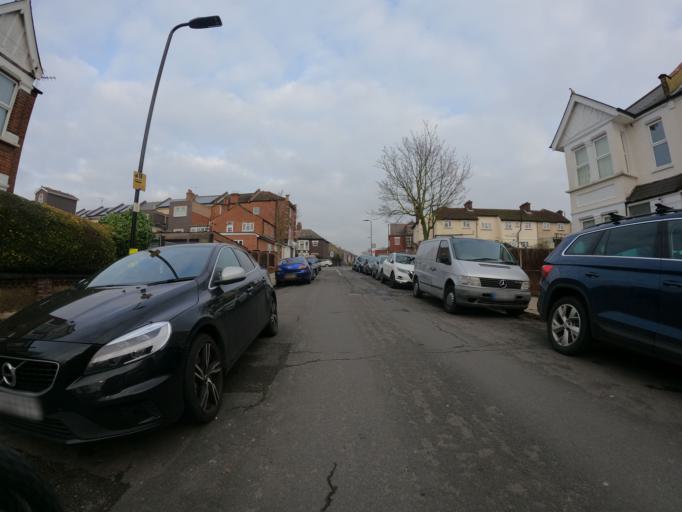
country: GB
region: England
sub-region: Greater London
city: Isleworth
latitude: 51.5033
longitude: -0.3333
